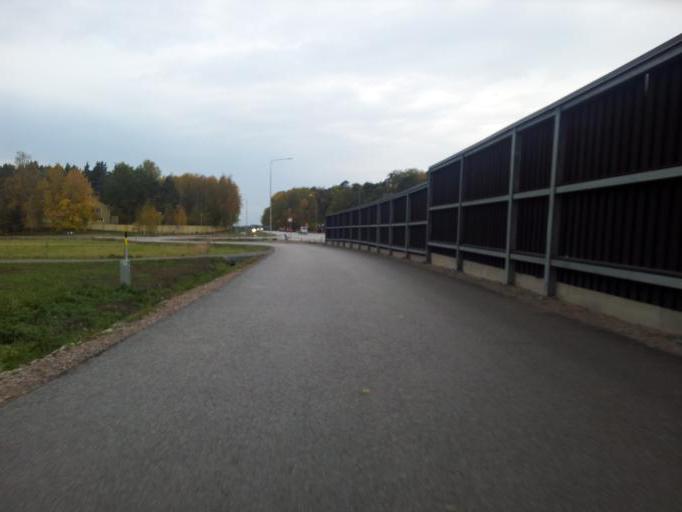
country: SE
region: Uppsala
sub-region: Uppsala Kommun
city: Storvreta
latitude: 59.9071
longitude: 17.7215
